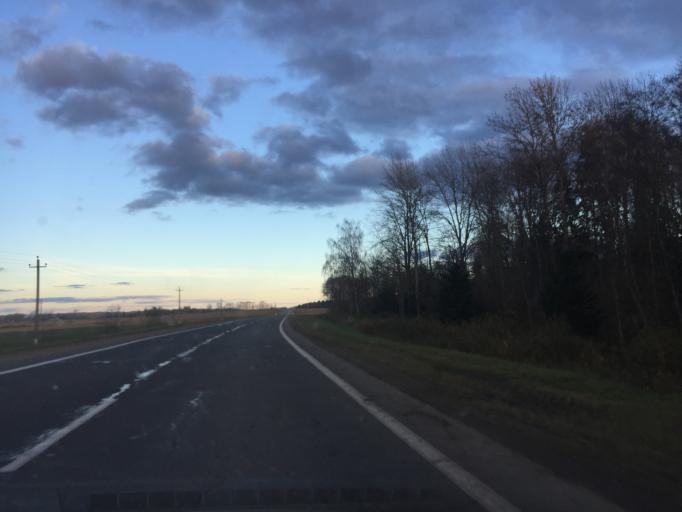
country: BY
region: Vitebsk
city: Myory
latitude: 55.8211
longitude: 27.7156
